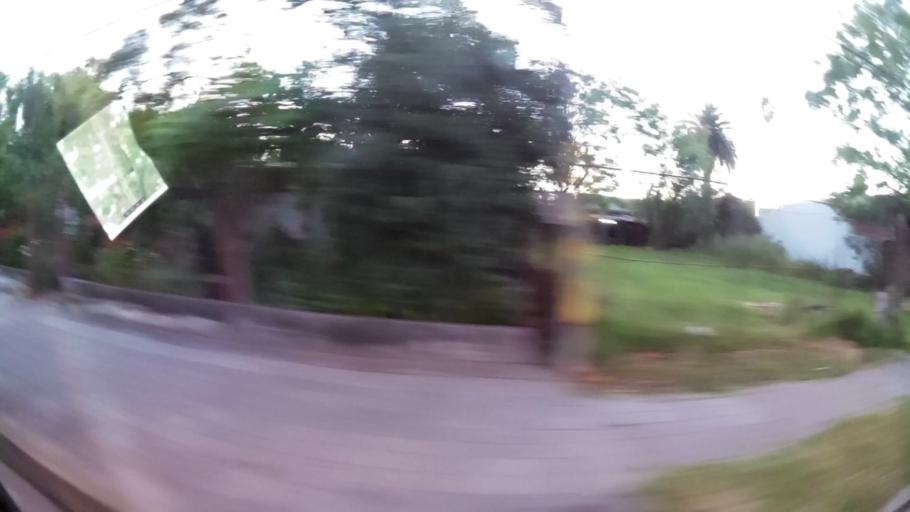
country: UY
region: Canelones
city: Paso de Carrasco
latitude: -34.8816
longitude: -56.0983
